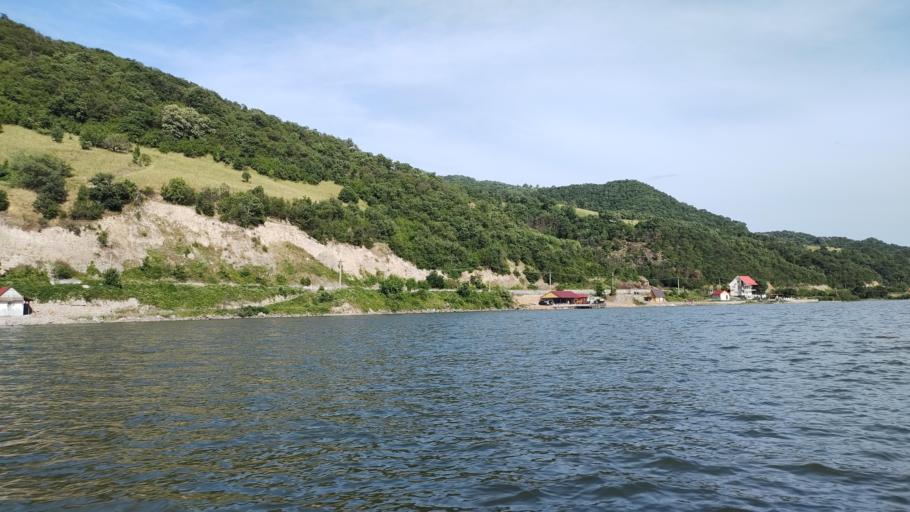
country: RO
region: Mehedinti
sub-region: Comuna Svinita
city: Svinita
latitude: 44.5625
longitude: 22.0307
